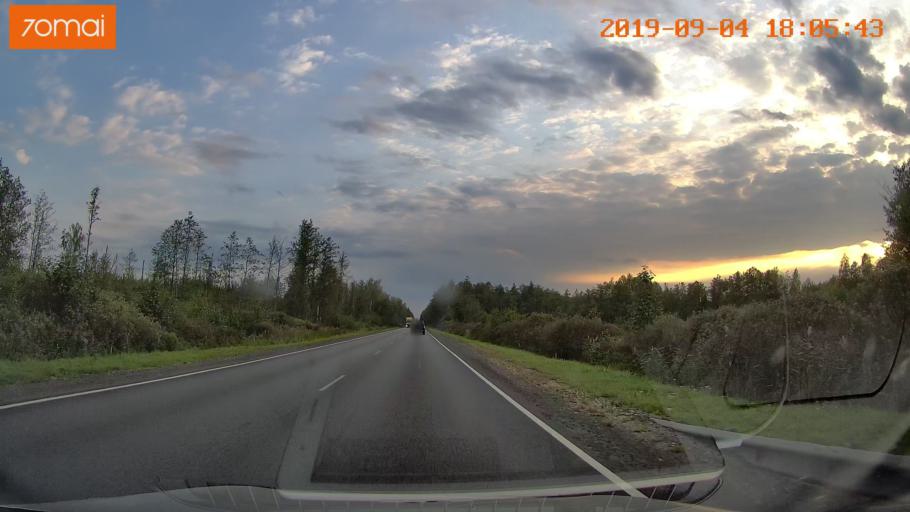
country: RU
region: Moskovskaya
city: Il'inskiy Pogost
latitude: 55.4385
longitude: 38.8233
